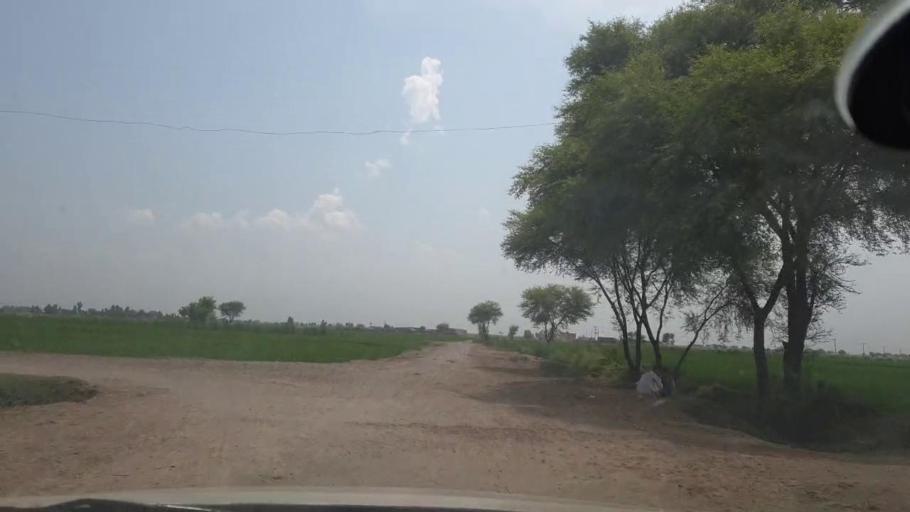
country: PK
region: Sindh
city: Jacobabad
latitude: 28.1367
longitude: 68.3743
